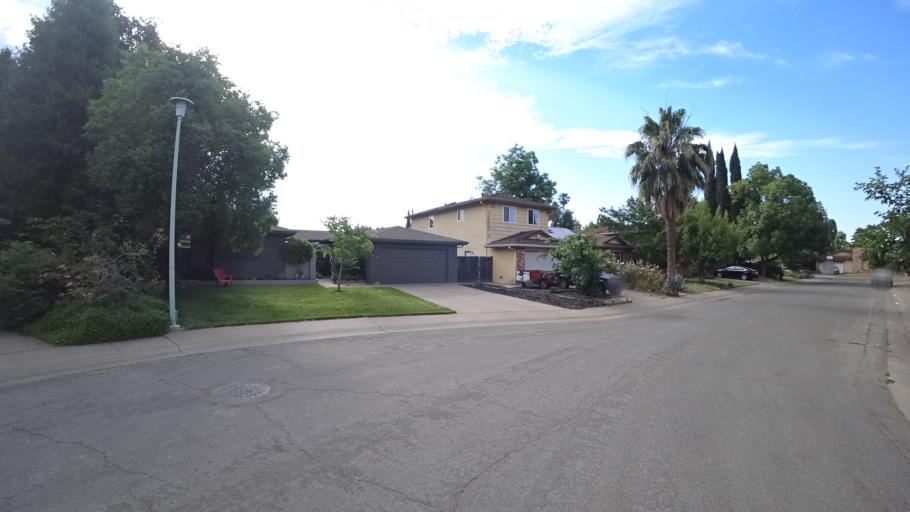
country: US
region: California
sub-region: Sacramento County
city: Rosemont
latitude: 38.5593
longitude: -121.3930
